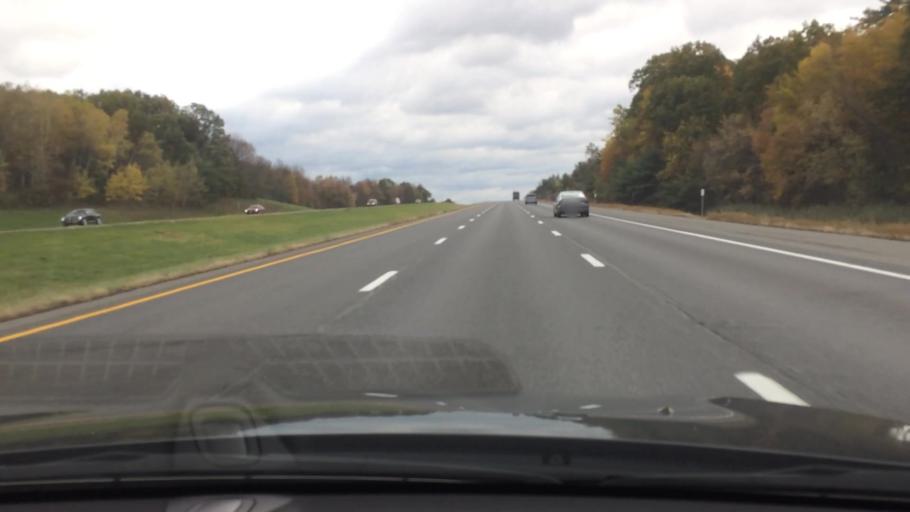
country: US
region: New York
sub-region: Rensselaer County
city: East Greenbush
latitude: 42.6090
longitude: -73.6861
